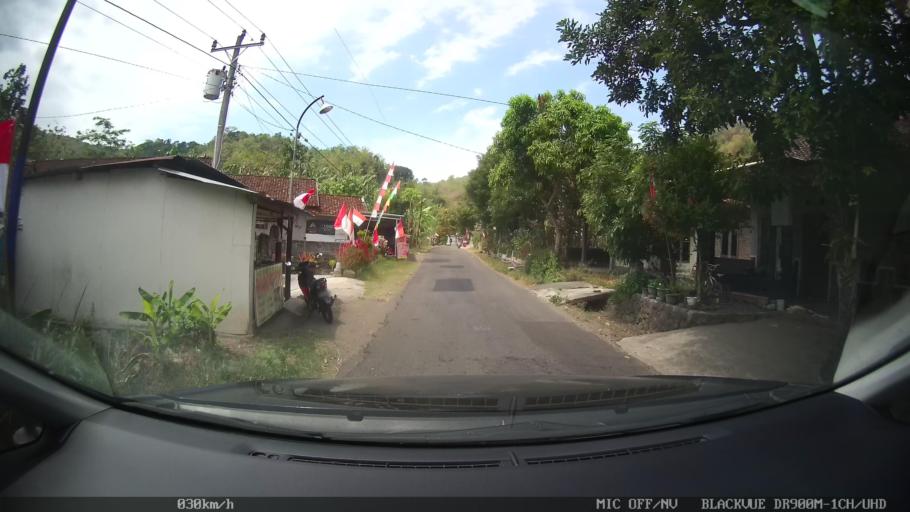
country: ID
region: Central Java
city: Candi Prambanan
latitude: -7.8127
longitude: 110.5116
